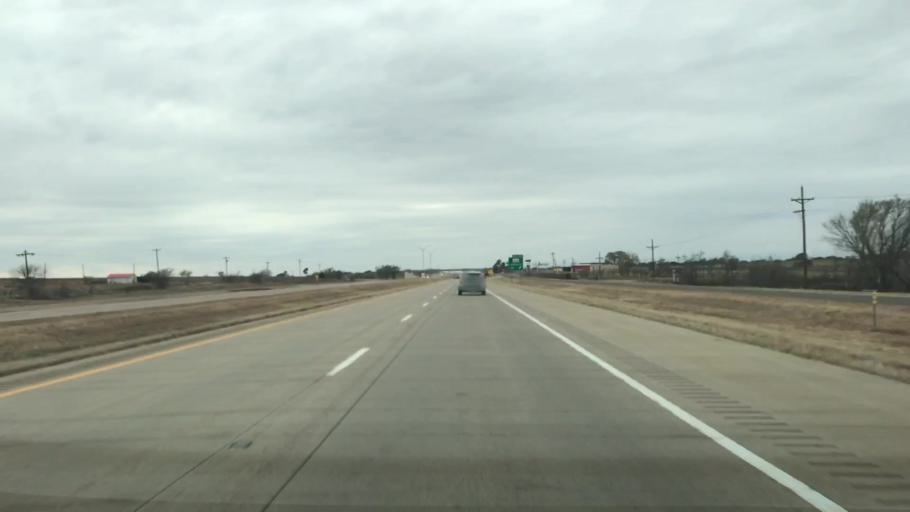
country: US
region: Texas
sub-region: Wheeler County
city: Shamrock
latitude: 35.2270
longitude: -100.1554
